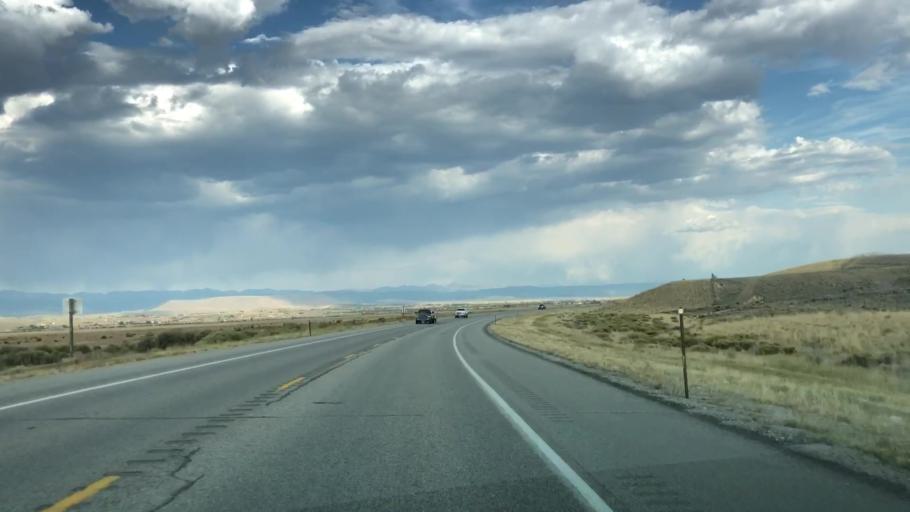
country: US
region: Wyoming
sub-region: Sublette County
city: Pinedale
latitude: 42.8748
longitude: -109.9438
